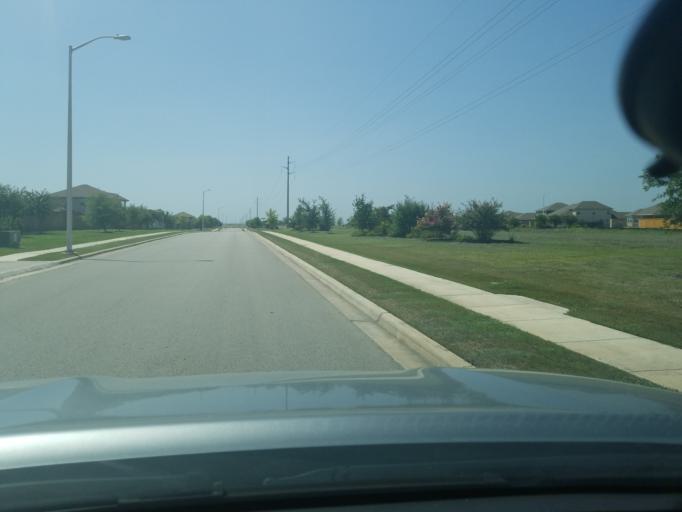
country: US
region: Texas
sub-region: Guadalupe County
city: Lake Dunlap
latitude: 29.6704
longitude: -98.0366
